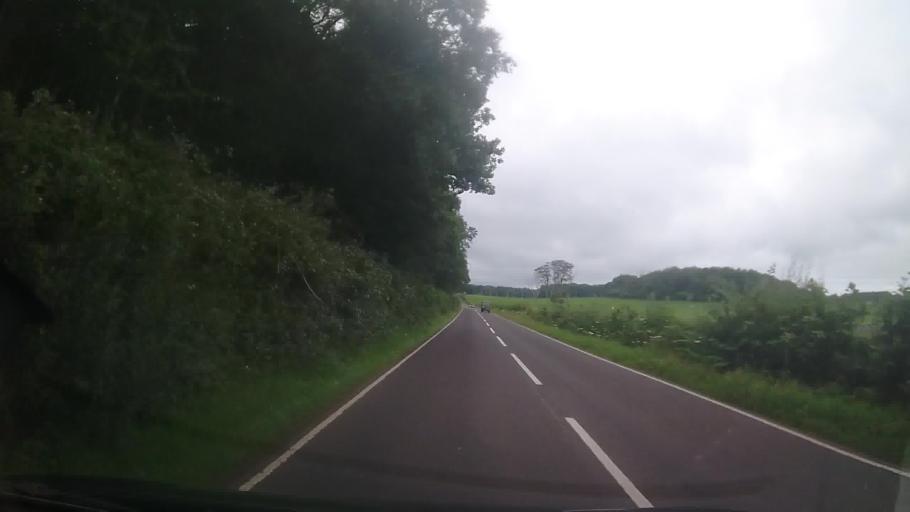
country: GB
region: Wales
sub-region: Anglesey
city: Llanfairpwllgwyngyll
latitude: 53.2131
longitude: -4.2133
